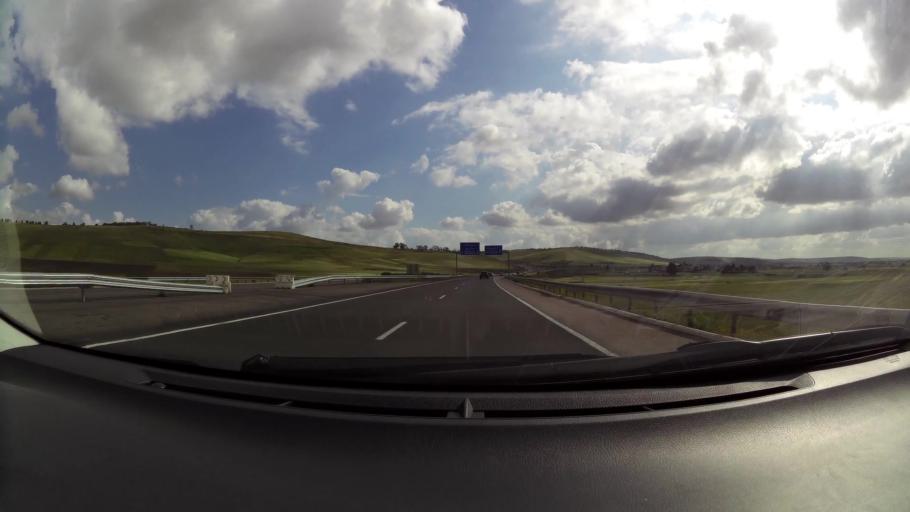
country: MA
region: Chaouia-Ouardigha
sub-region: Settat Province
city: Settat
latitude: 33.0820
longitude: -7.5908
